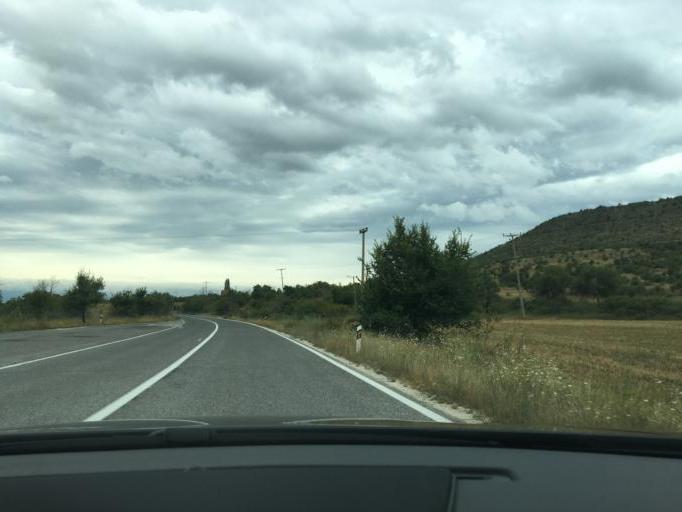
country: MK
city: Klechovce
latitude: 42.1484
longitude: 21.9752
